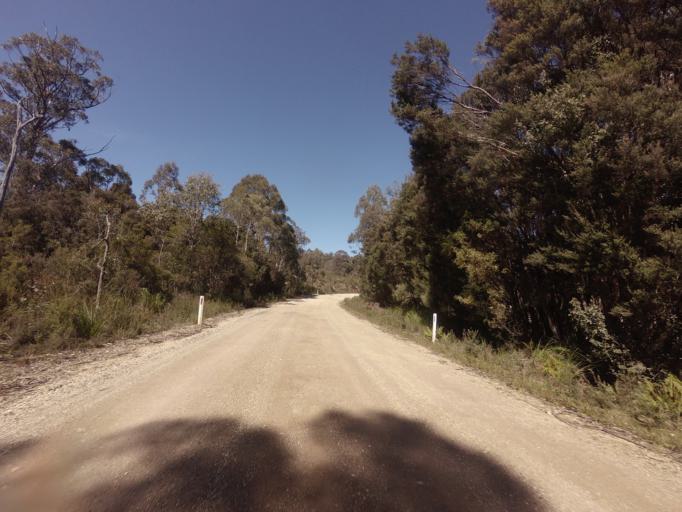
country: AU
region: Tasmania
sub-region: Huon Valley
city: Geeveston
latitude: -42.9054
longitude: 146.3694
